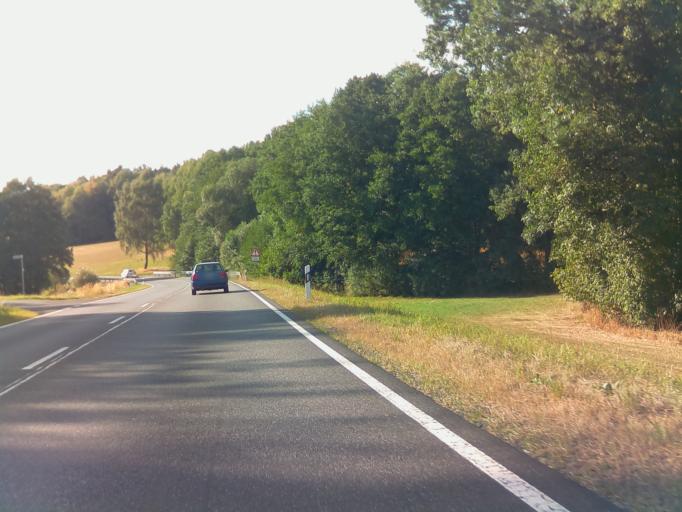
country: DE
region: Hesse
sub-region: Regierungsbezirk Kassel
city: Poppenhausen
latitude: 50.5129
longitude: 9.8644
